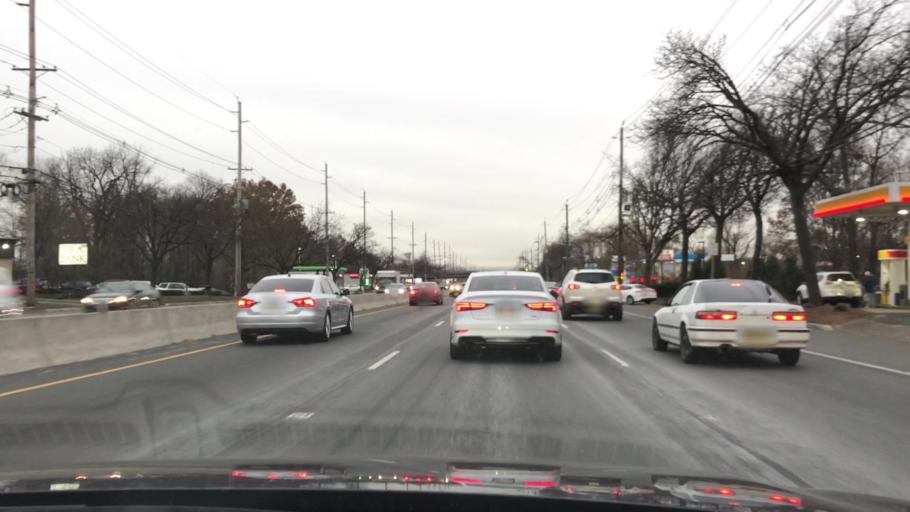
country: US
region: New Jersey
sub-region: Bergen County
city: Paramus
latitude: 40.9636
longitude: -74.0770
